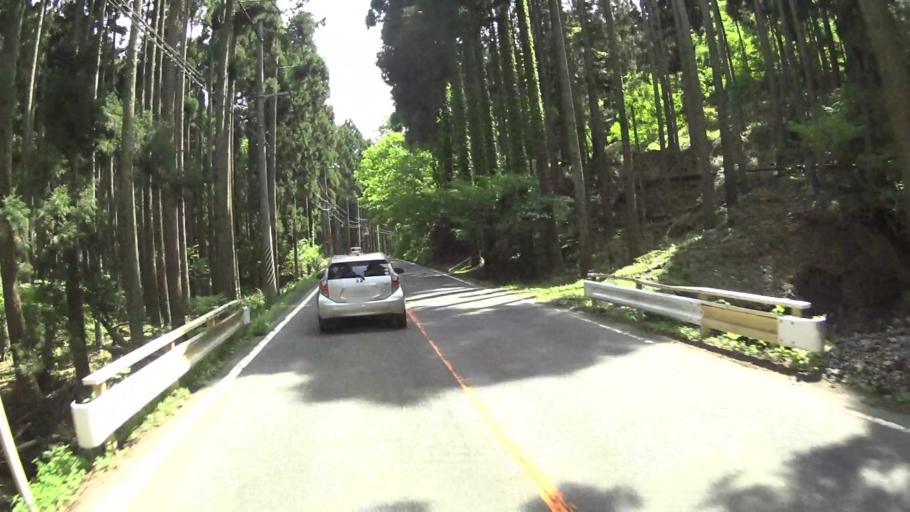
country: JP
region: Shiga Prefecture
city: Kitahama
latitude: 35.3708
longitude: 135.9214
